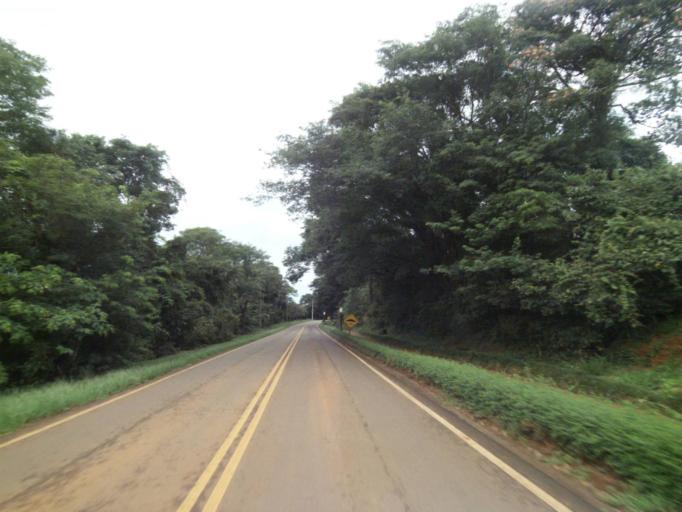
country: BR
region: Parana
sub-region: Guaraniacu
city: Guaraniacu
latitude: -25.0981
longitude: -52.8865
